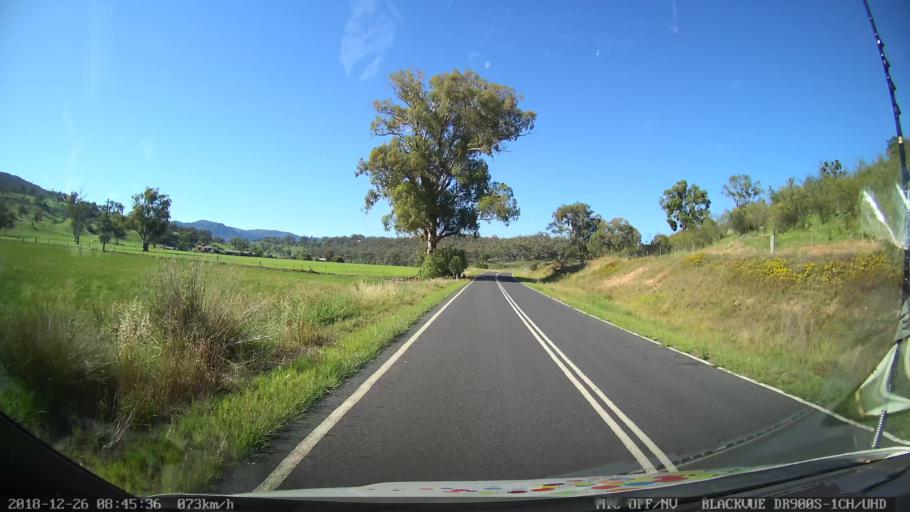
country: AU
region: New South Wales
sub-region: Mid-Western Regional
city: Kandos
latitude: -32.5270
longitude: 150.0869
